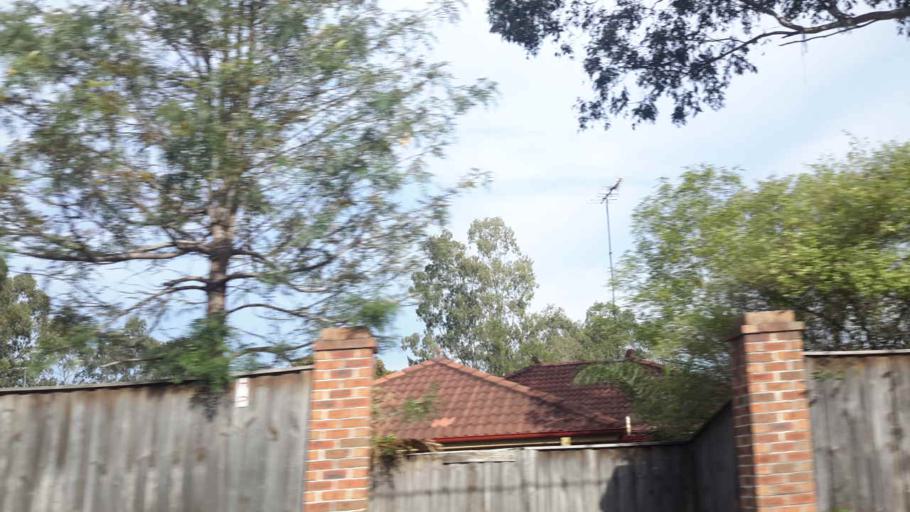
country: AU
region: New South Wales
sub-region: Penrith Municipality
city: Cambridge Park
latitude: -33.7536
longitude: 150.7128
